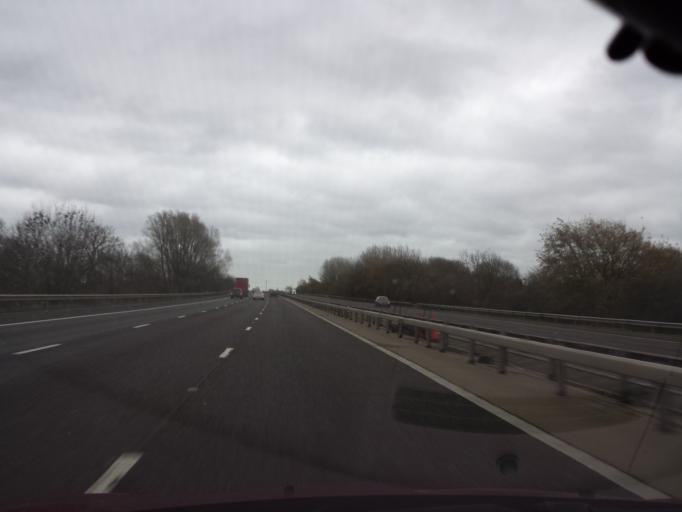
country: GB
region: England
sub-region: Surrey
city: Chertsey
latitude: 51.3949
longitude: -0.4937
